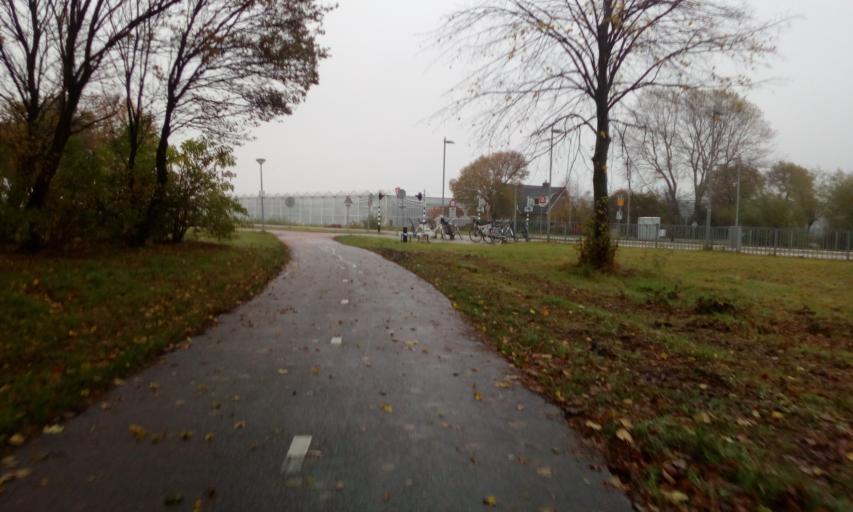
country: NL
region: South Holland
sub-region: Gemeente Lansingerland
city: Bergschenhoek
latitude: 52.0067
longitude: 4.5017
